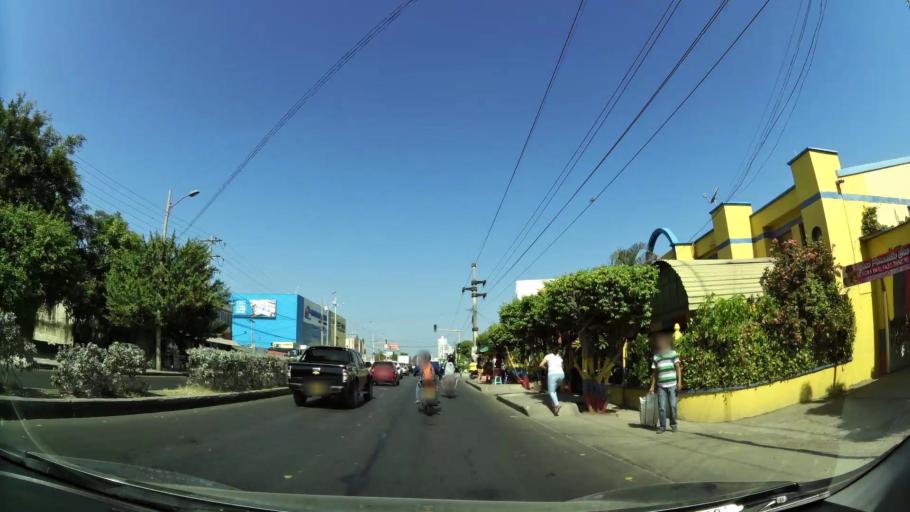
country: CO
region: Bolivar
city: Cartagena
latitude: 10.3833
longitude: -75.4675
